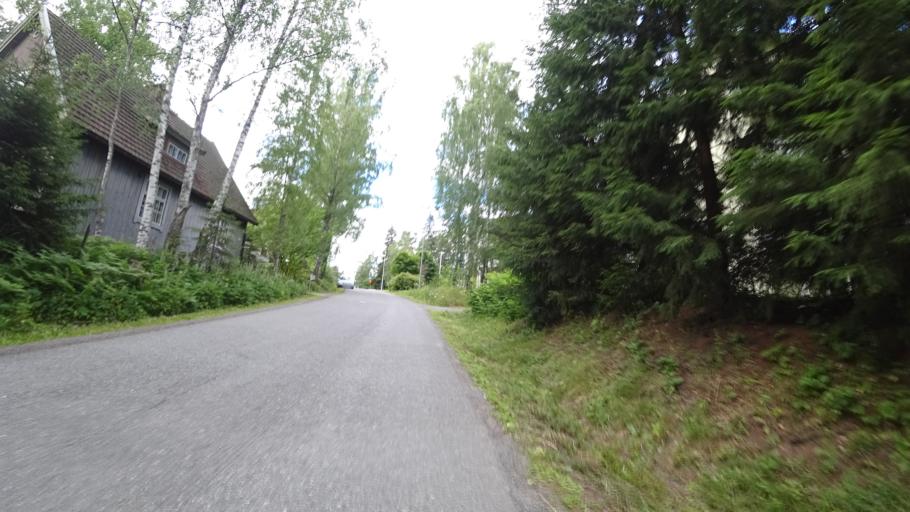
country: FI
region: Pirkanmaa
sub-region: Tampere
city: Pirkkala
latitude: 61.4940
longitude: 23.5864
